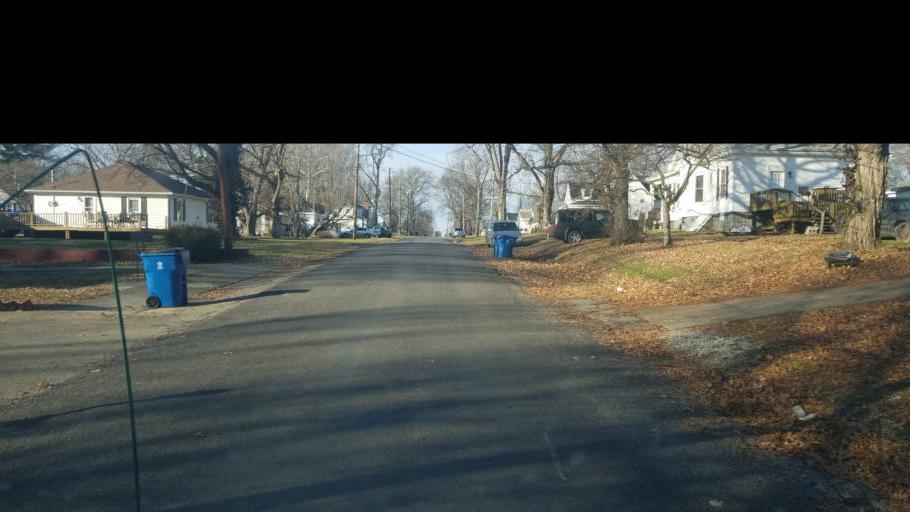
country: US
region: Illinois
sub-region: Wabash County
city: Mount Carmel
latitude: 38.4150
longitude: -87.7565
